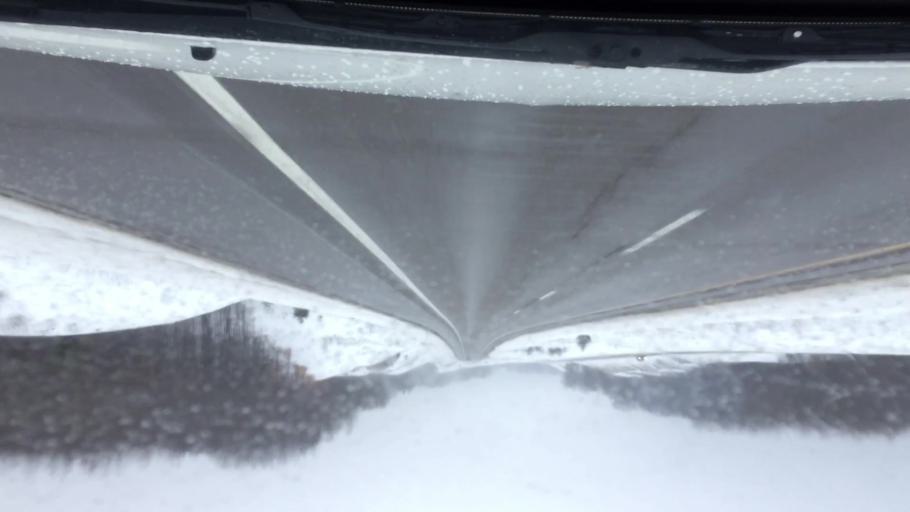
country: US
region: Michigan
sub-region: Wexford County
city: Manton
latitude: 44.3416
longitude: -85.4057
